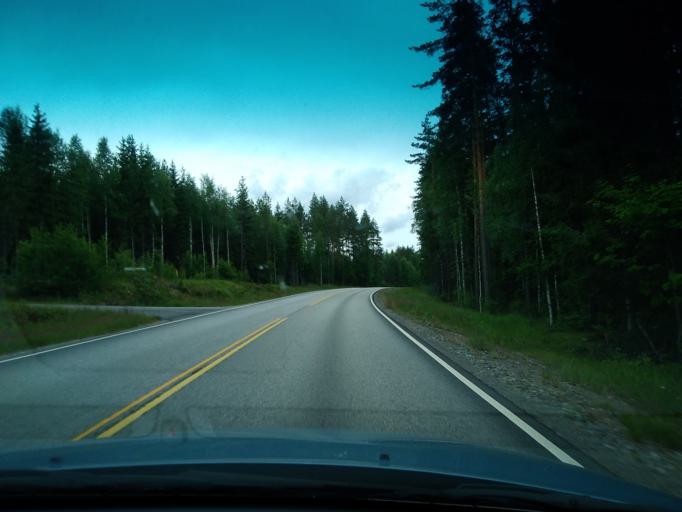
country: FI
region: Central Finland
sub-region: Keuruu
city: Multia
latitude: 62.4887
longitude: 24.6941
